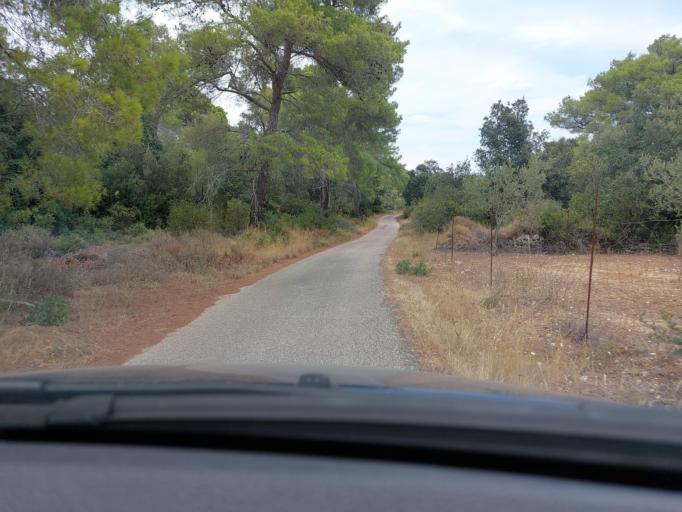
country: HR
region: Dubrovacko-Neretvanska
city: Smokvica
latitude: 42.7588
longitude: 16.9319
